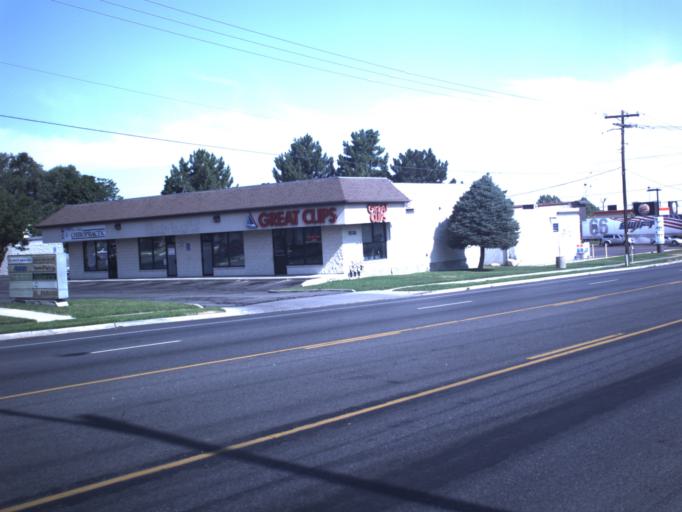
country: US
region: Utah
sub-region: Salt Lake County
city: West Valley City
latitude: 40.6954
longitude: -112.0248
